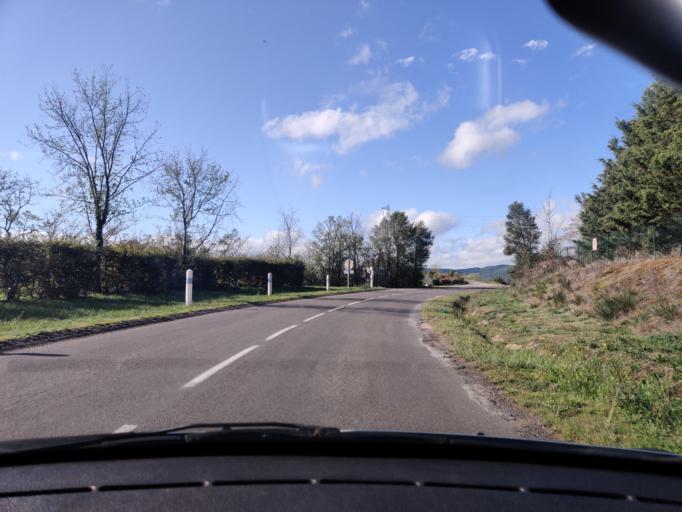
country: FR
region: Auvergne
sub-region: Departement du Puy-de-Dome
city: Combronde
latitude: 45.9900
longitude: 3.1221
